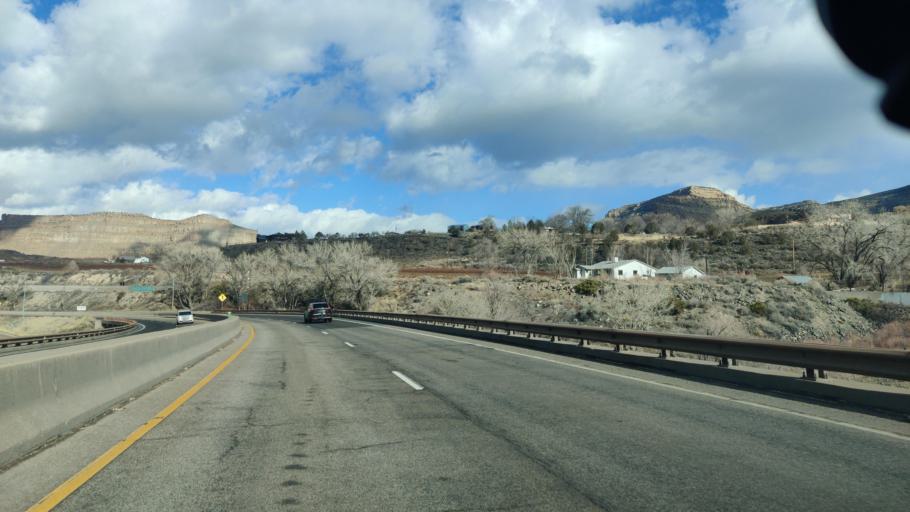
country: US
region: Colorado
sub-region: Mesa County
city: Palisade
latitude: 39.1235
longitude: -108.3224
